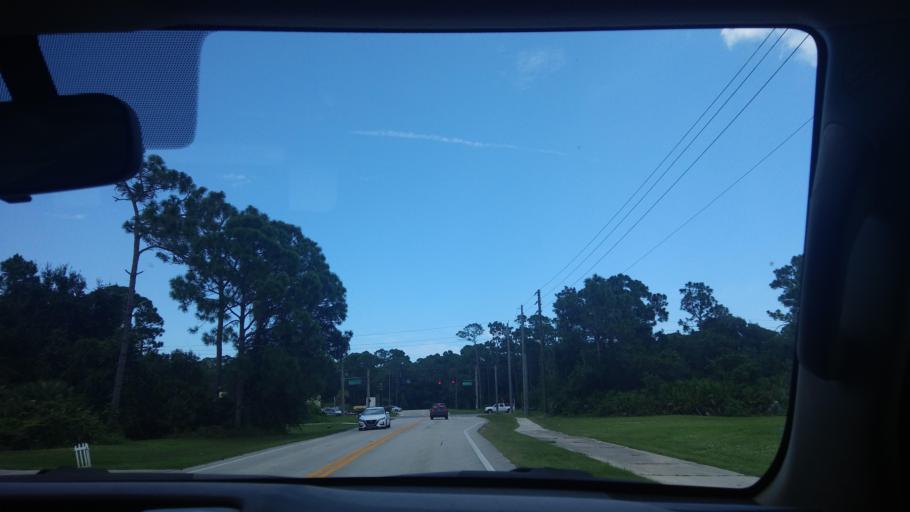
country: US
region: Florida
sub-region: Brevard County
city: Grant-Valkaria
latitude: 27.9661
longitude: -80.6238
